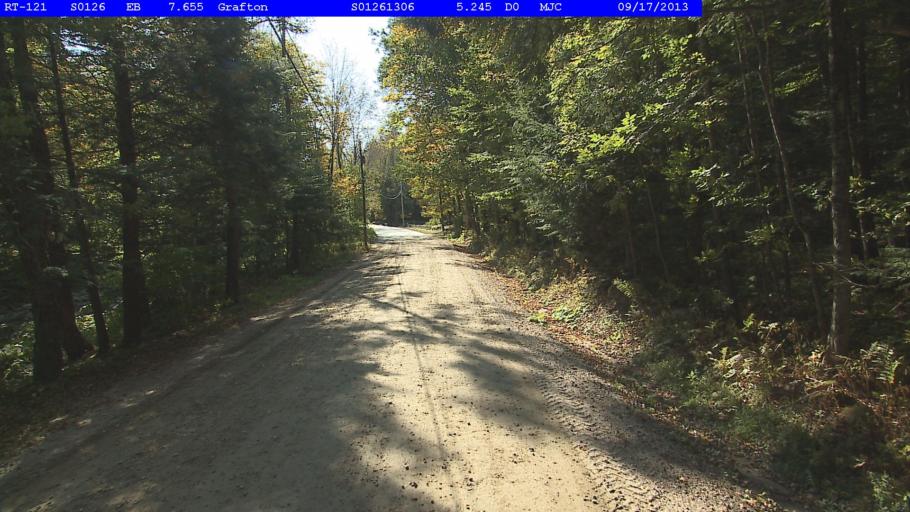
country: US
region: Vermont
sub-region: Windsor County
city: Chester
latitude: 43.1760
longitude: -72.6120
